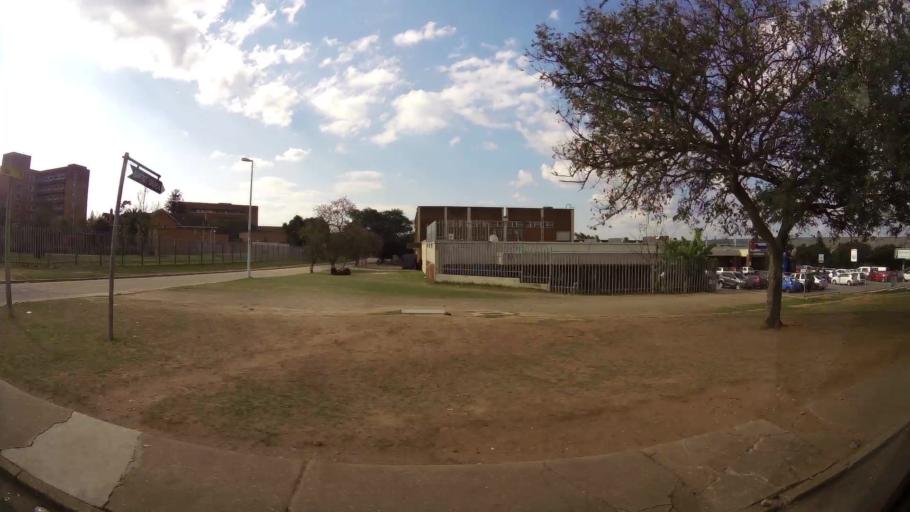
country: ZA
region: Eastern Cape
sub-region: Nelson Mandela Bay Metropolitan Municipality
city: Uitenhage
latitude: -33.7434
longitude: 25.4077
